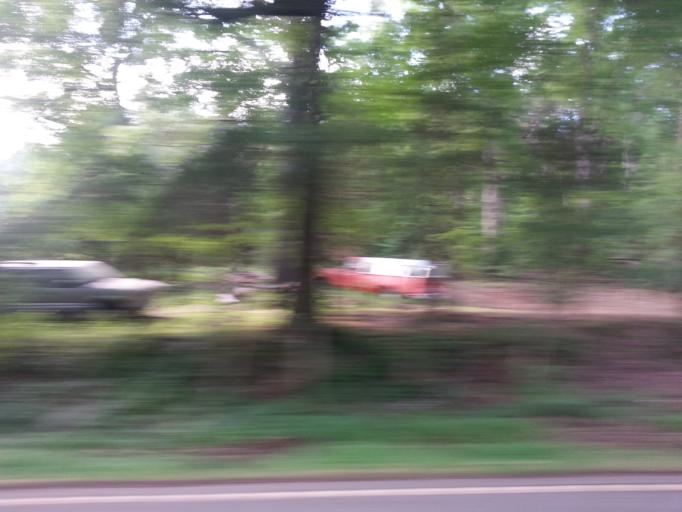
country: US
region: Tennessee
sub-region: Loudon County
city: Greenback
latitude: 35.6078
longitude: -84.0708
